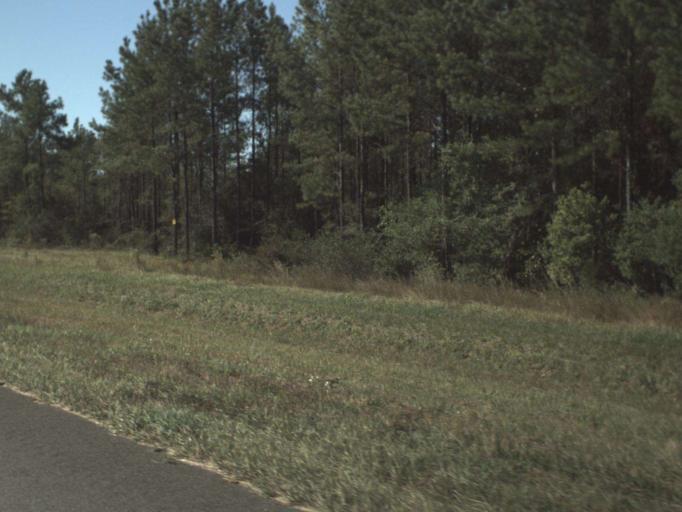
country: US
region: Florida
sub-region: Walton County
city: Freeport
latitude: 30.5290
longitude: -86.1081
